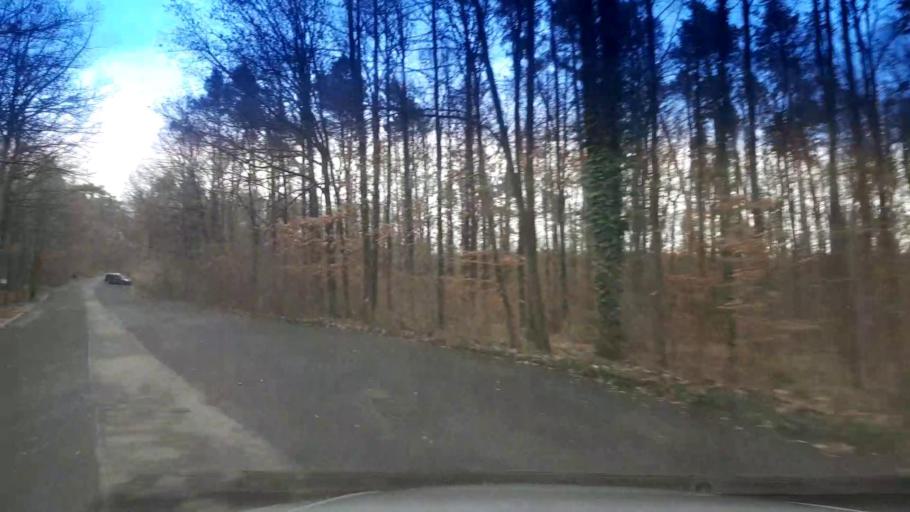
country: DE
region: Bavaria
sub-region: Upper Franconia
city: Bischberg
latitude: 49.8967
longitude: 10.8560
